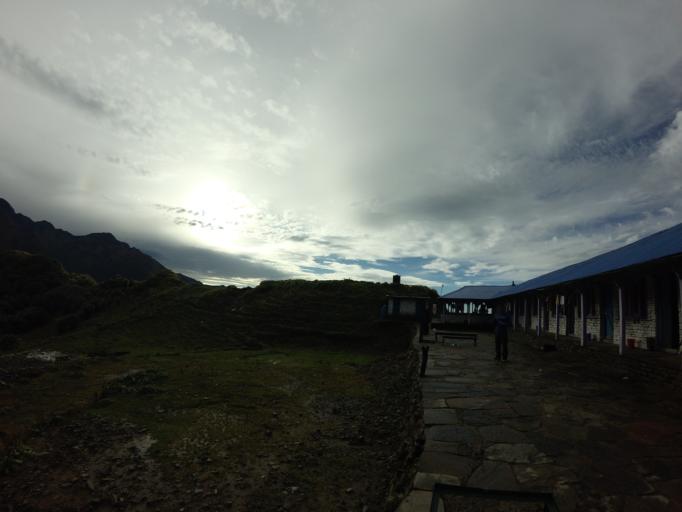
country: NP
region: Western Region
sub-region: Dhawalagiri Zone
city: Chitre
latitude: 28.4339
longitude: 83.8682
